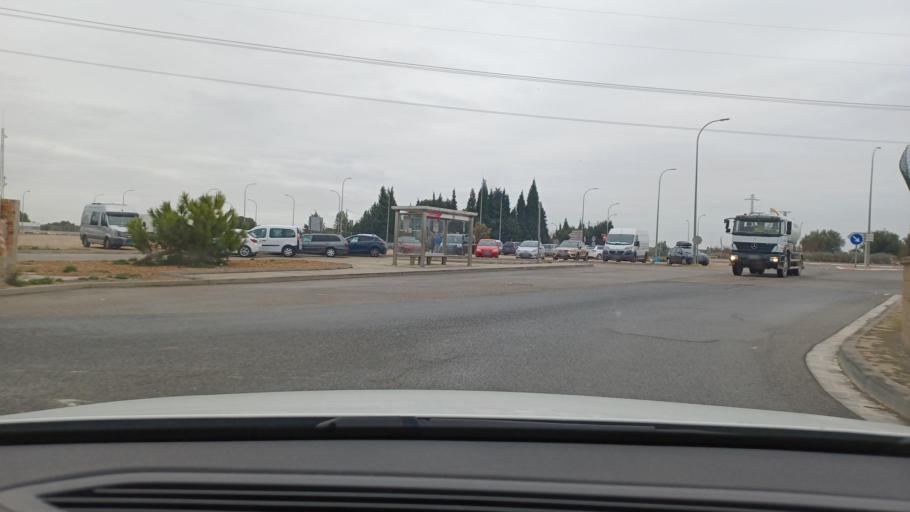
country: ES
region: Catalonia
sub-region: Provincia de Tarragona
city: Amposta
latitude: 40.7552
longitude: 0.6000
